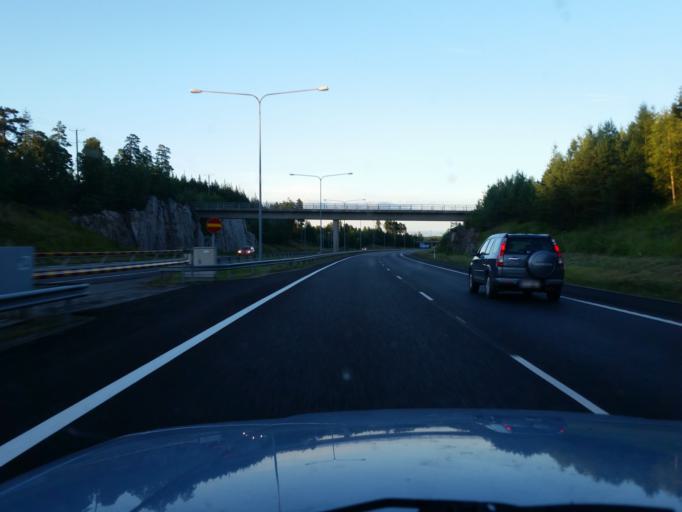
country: FI
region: Varsinais-Suomi
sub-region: Turku
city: Paimio
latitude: 60.4261
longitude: 22.7102
